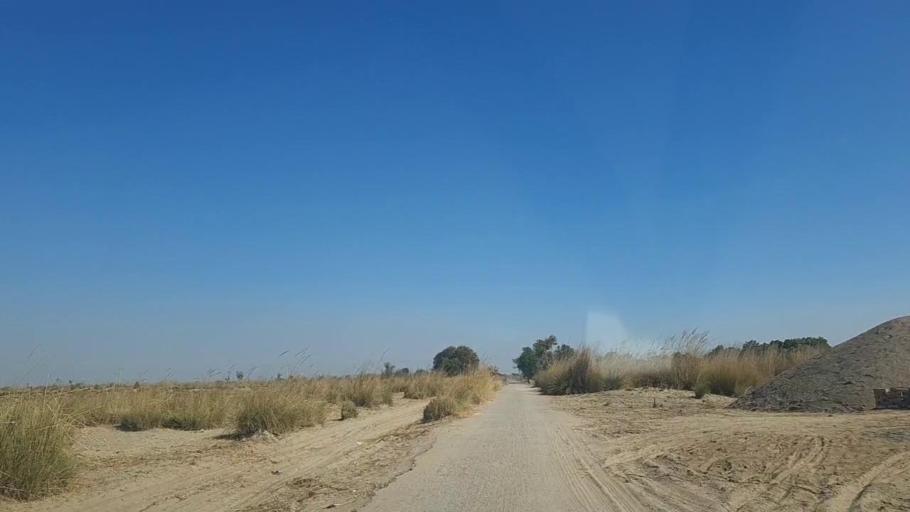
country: PK
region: Sindh
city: Khadro
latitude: 26.2092
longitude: 68.8678
